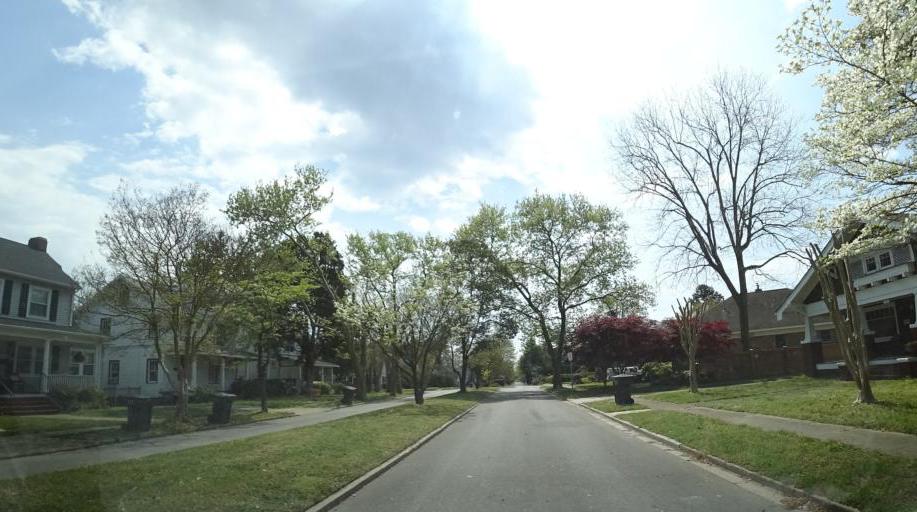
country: US
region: Virginia
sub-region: City of Hampton
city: Hampton
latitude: 37.0030
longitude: -76.3760
